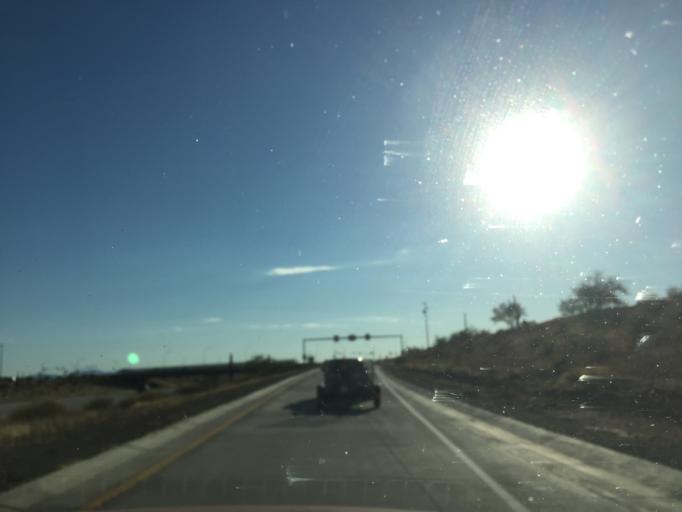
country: US
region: Arizona
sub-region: Maricopa County
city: Anthem
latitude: 33.7717
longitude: -112.2462
